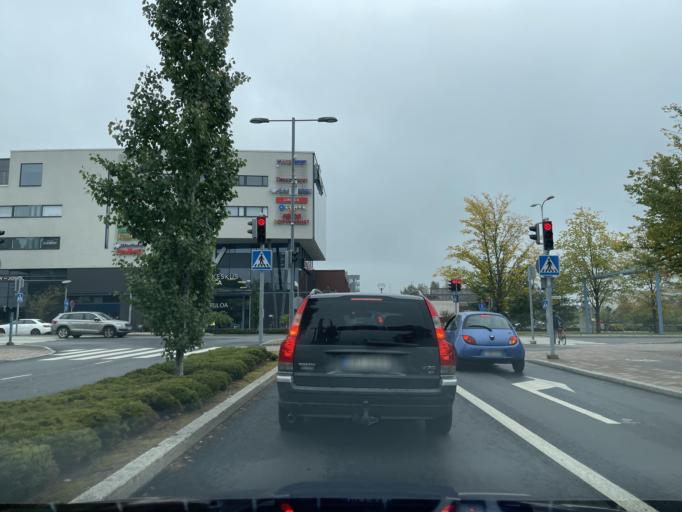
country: FI
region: Uusimaa
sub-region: Helsinki
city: Hyvinge
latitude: 60.6324
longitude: 24.8614
